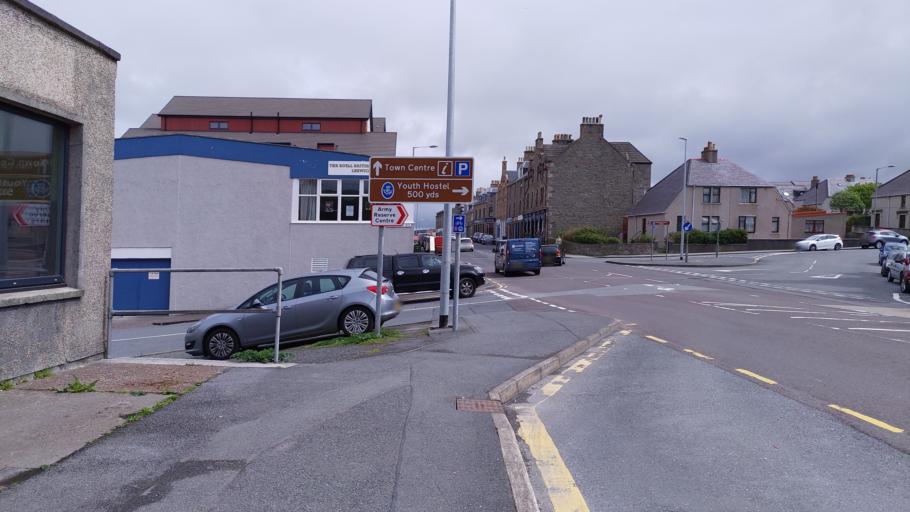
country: GB
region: Scotland
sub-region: Shetland Islands
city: Lerwick
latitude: 60.1570
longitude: -1.1522
